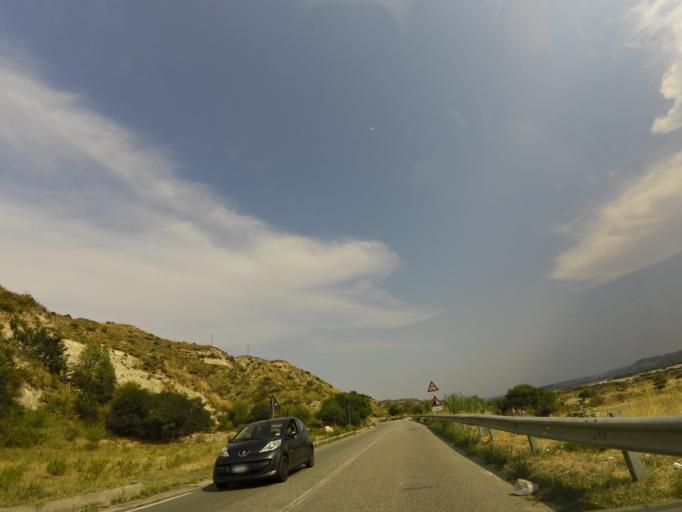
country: IT
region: Calabria
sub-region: Provincia di Reggio Calabria
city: Monasterace
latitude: 38.4642
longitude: 16.5138
